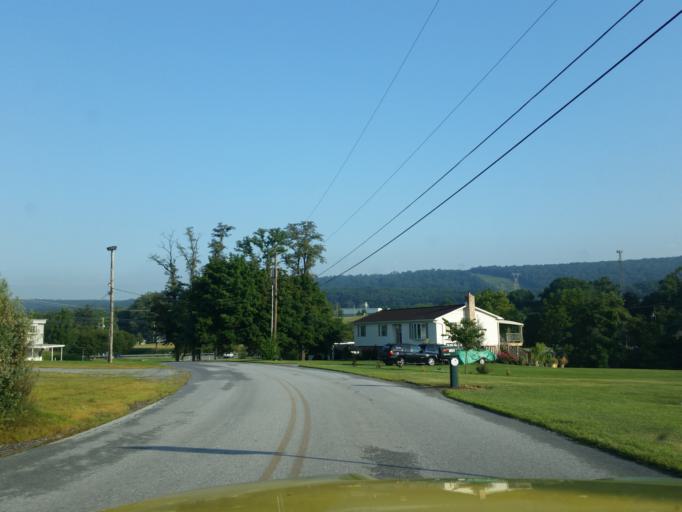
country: US
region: Pennsylvania
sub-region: York County
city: Stonybrook
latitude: 39.9942
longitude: -76.6294
